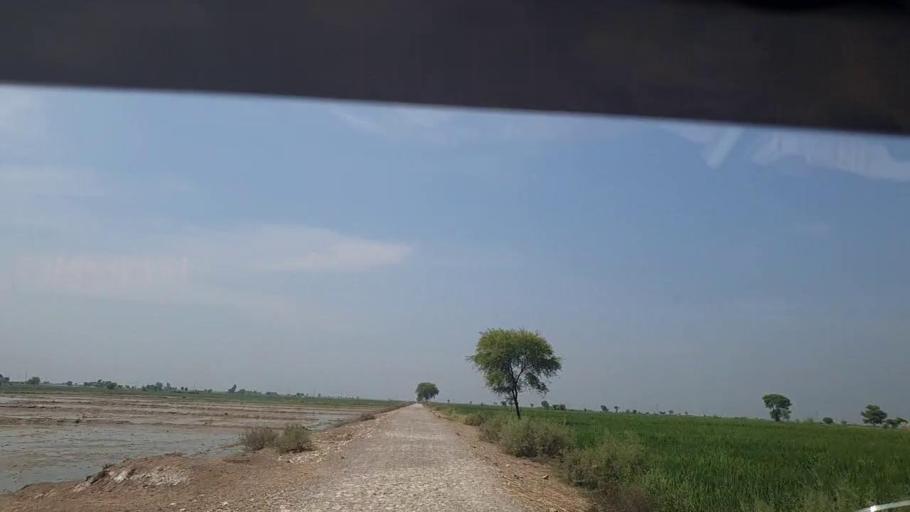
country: PK
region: Sindh
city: Thul
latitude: 28.2112
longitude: 68.6867
